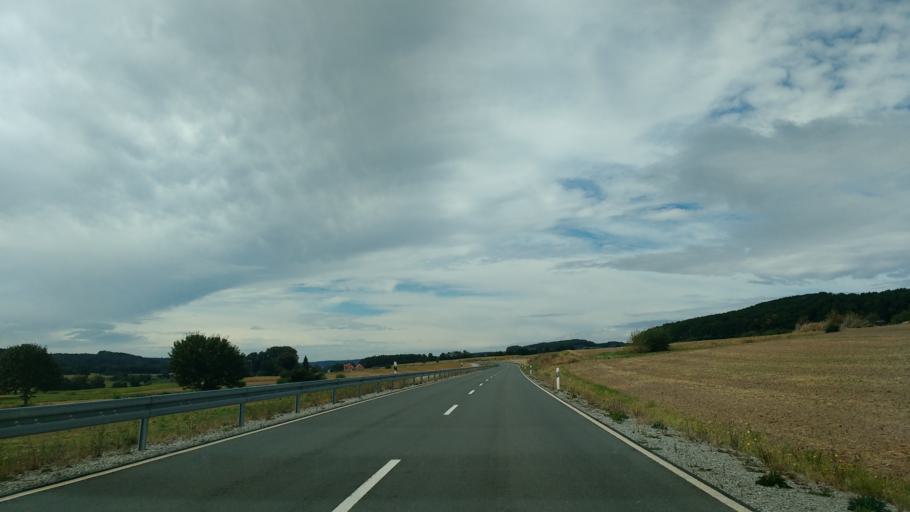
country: DE
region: Bavaria
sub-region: Regierungsbezirk Mittelfranken
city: Burghaslach
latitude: 49.7666
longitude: 10.5584
